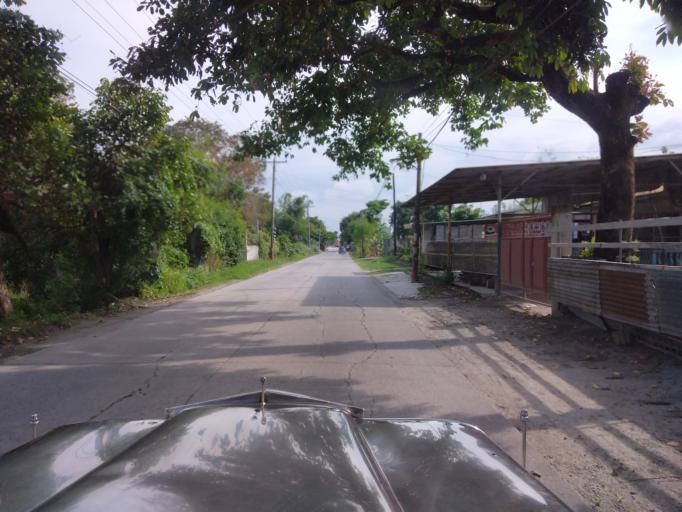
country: PH
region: Central Luzon
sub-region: Province of Pampanga
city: San Patricio
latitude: 15.0977
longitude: 120.7102
